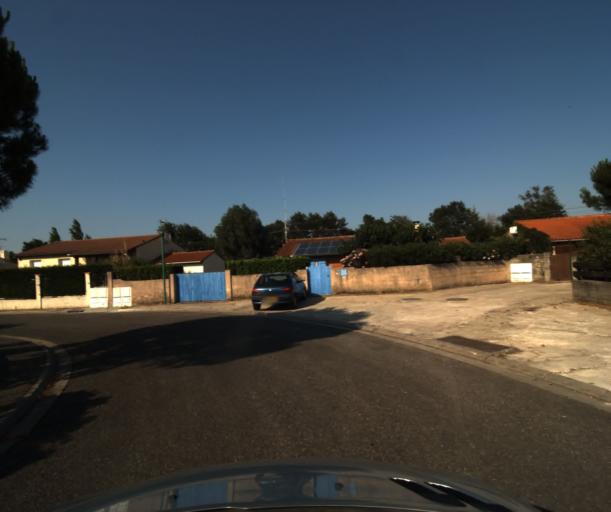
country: FR
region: Midi-Pyrenees
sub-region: Departement de la Haute-Garonne
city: Labarthe-sur-Leze
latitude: 43.4754
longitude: 1.4007
